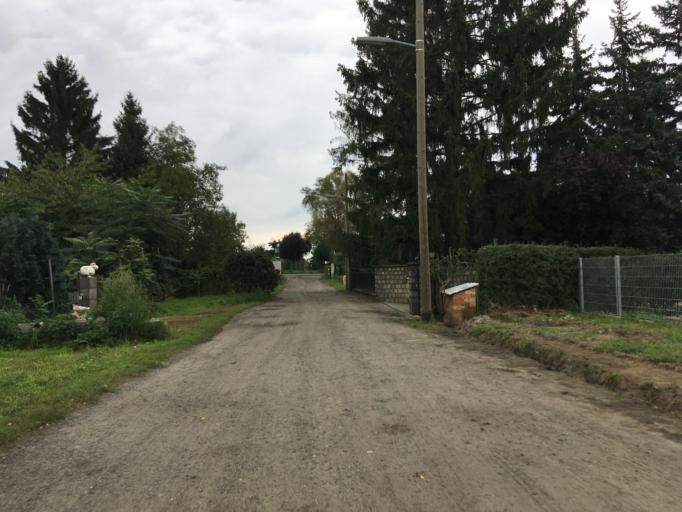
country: DE
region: Berlin
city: Biesdorf
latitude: 52.4894
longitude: 13.5546
